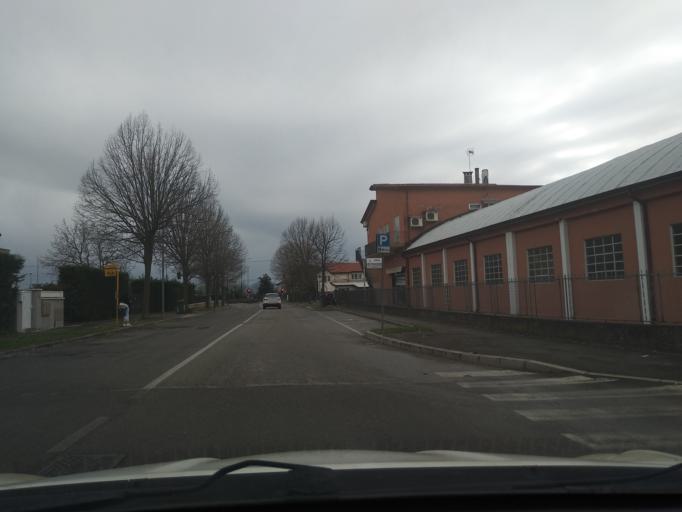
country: IT
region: Veneto
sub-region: Provincia di Padova
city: Selvazzano Dentro
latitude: 45.3859
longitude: 11.7845
